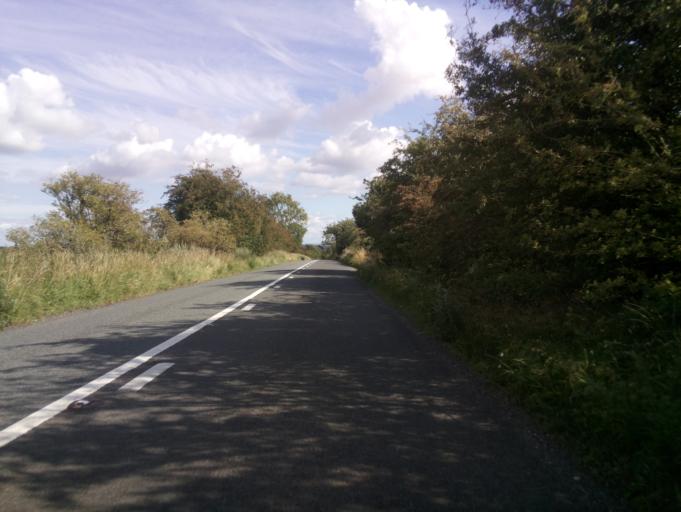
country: GB
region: England
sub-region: Gloucestershire
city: Cirencester
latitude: 51.7391
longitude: -1.9894
